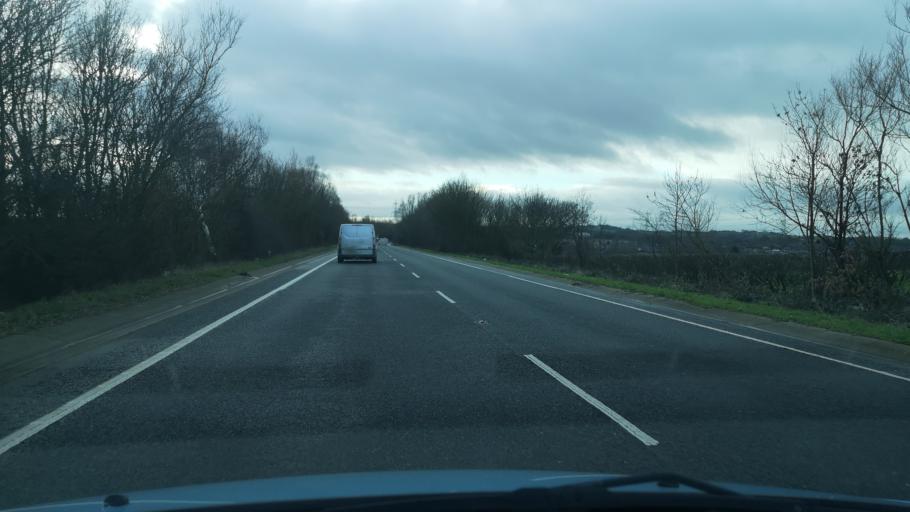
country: GB
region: England
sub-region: City and Borough of Wakefield
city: Hemsworth
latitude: 53.6149
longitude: -1.3354
